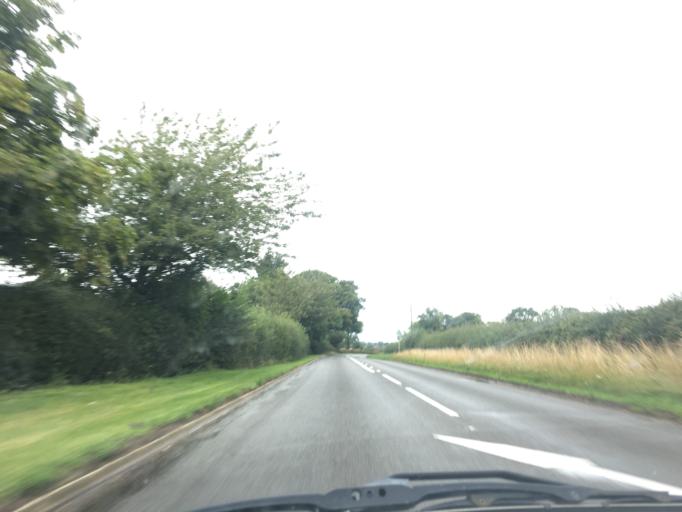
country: GB
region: England
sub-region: Leicestershire
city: Sapcote
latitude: 52.5072
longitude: -1.3151
